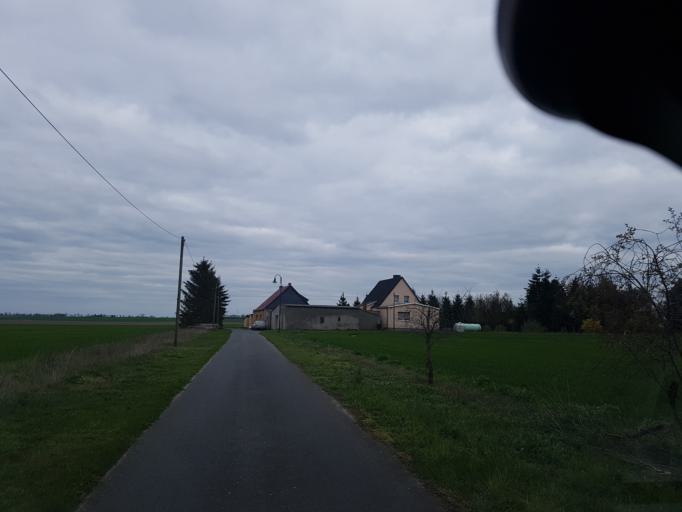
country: DE
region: Brandenburg
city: Juterbog
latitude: 51.9128
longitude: 13.1001
